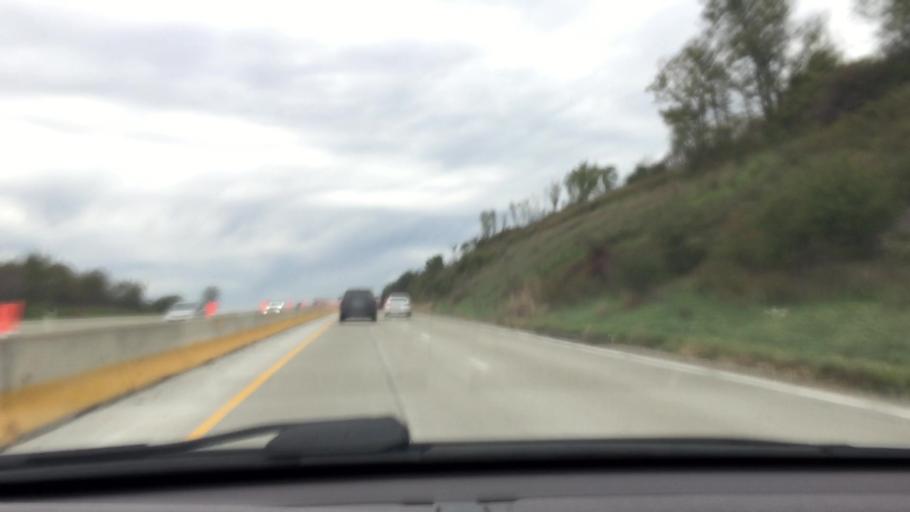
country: US
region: Pennsylvania
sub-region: Allegheny County
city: Enlow
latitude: 40.4710
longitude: -80.2467
